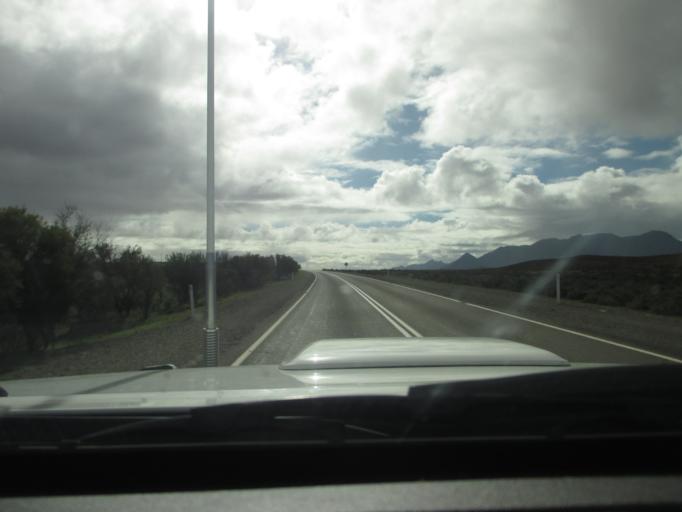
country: AU
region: South Australia
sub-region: Flinders Ranges
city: Quorn
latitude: -31.5881
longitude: 138.4149
